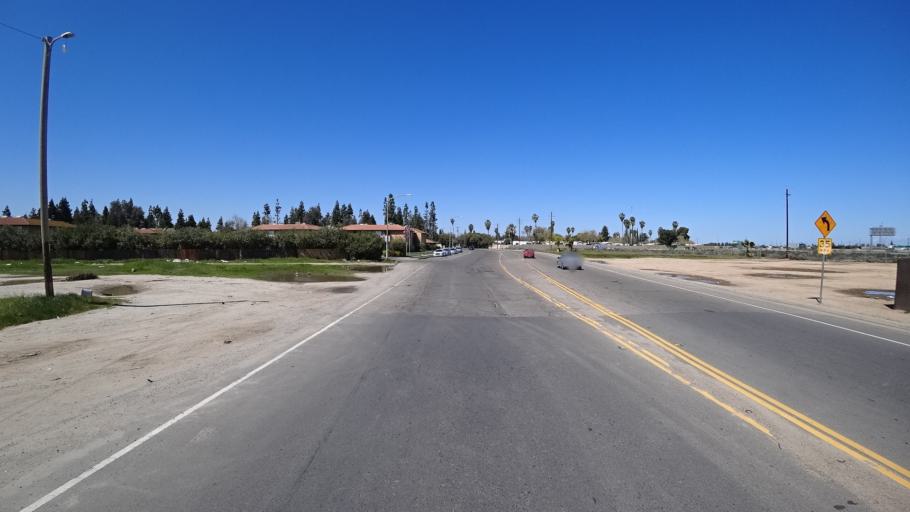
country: US
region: California
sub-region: Fresno County
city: West Park
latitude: 36.7785
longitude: -119.8473
